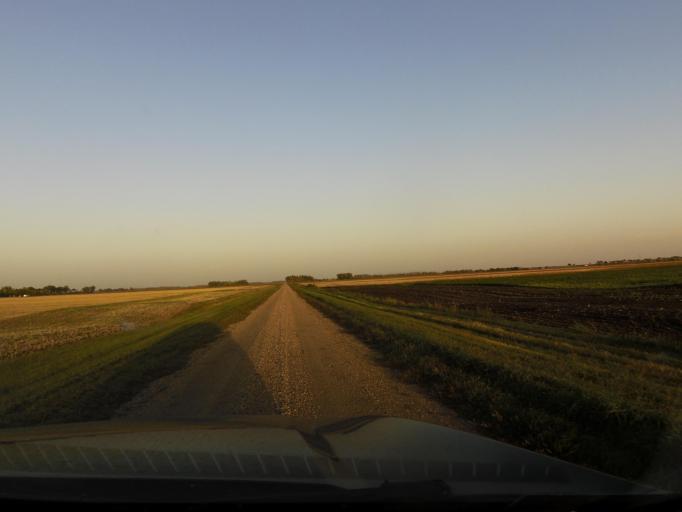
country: US
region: North Dakota
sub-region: Walsh County
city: Grafton
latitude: 48.3833
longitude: -97.2222
